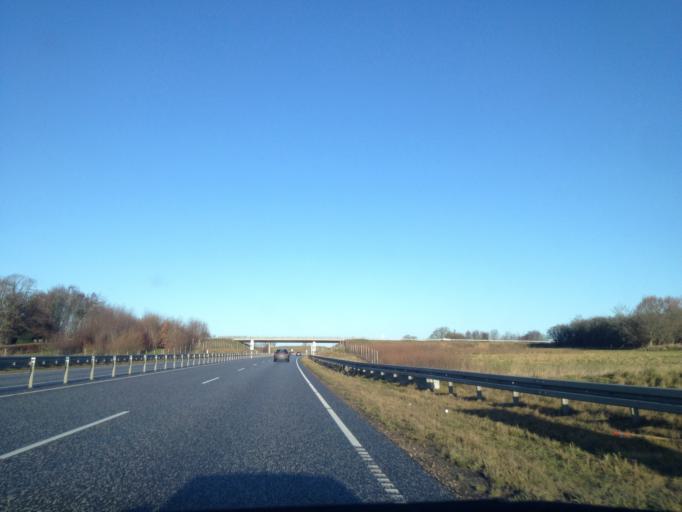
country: DK
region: Zealand
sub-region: Odsherred Kommune
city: Asnaes
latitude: 55.8001
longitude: 11.5810
